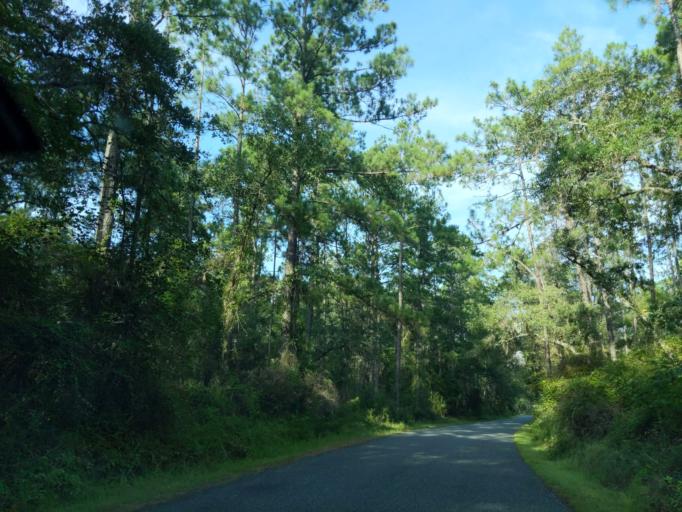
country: US
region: Florida
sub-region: Leon County
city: Woodville
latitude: 30.3448
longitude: -84.3805
